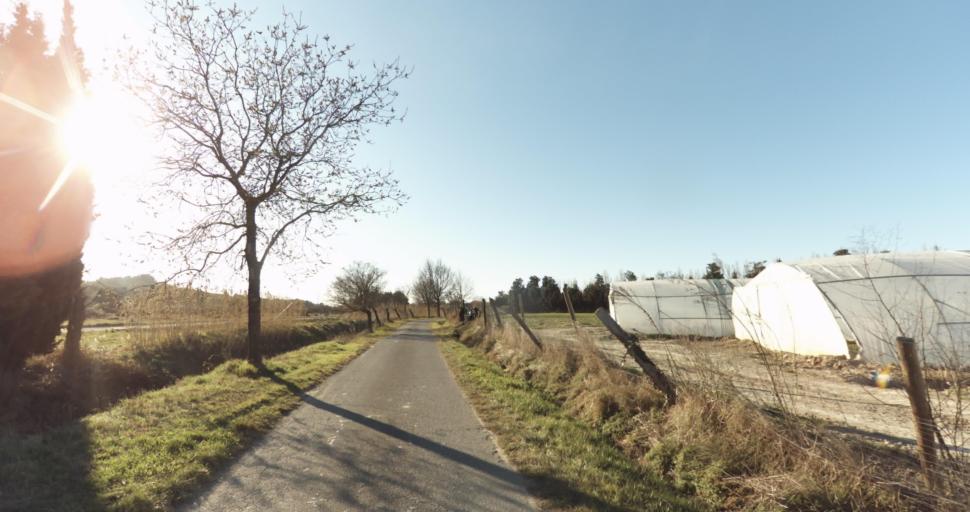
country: FR
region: Provence-Alpes-Cote d'Azur
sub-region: Departement des Bouches-du-Rhone
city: Barbentane
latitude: 43.9018
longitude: 4.7363
